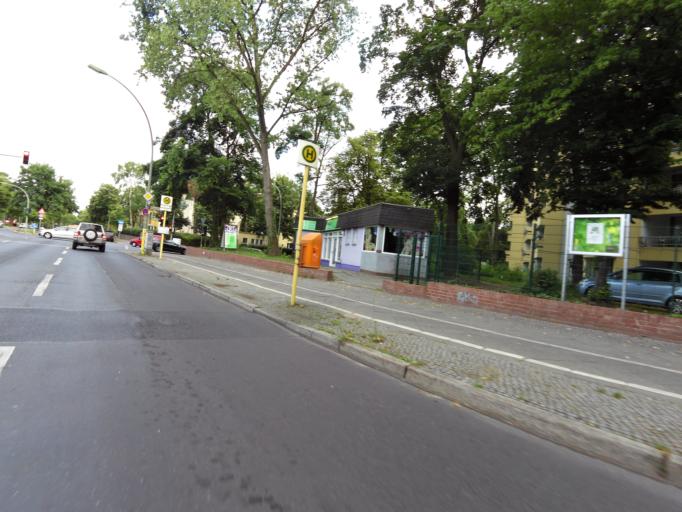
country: DE
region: Berlin
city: Lichterfelde
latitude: 52.4337
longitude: 13.3069
